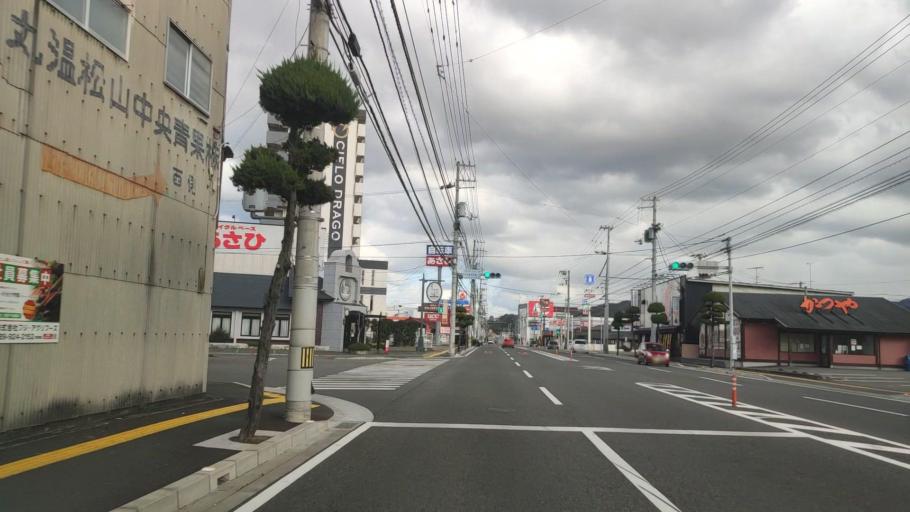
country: JP
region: Ehime
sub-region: Shikoku-chuo Shi
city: Matsuyama
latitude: 33.8617
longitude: 132.7496
